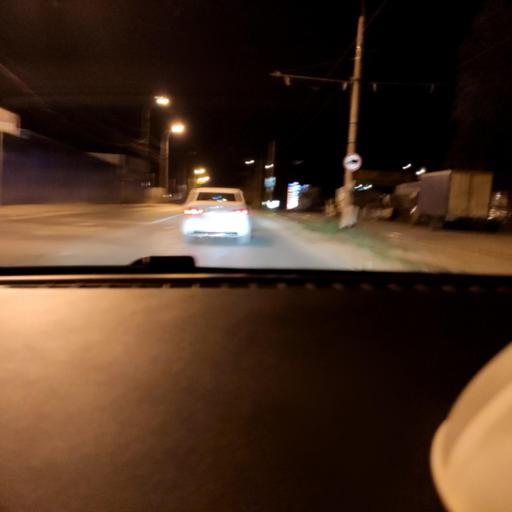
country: RU
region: Samara
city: Petra-Dubrava
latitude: 53.2269
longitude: 50.2804
